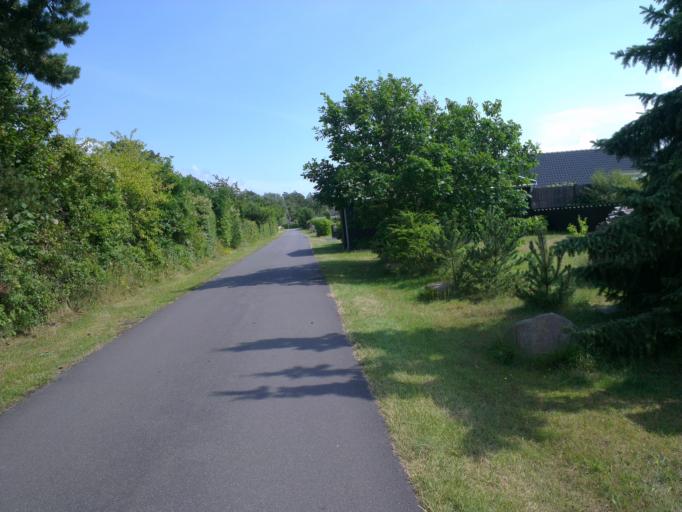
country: DK
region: Capital Region
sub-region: Halsnaes Kommune
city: Hundested
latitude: 55.9157
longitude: 11.9075
